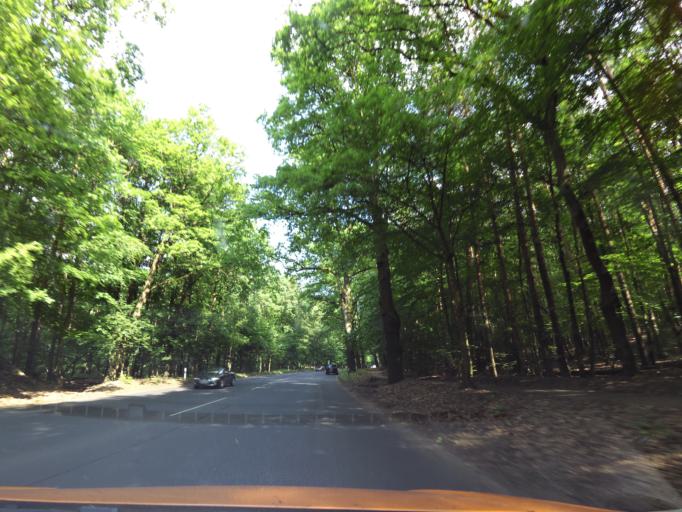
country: DE
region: Berlin
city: Heiligensee
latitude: 52.5993
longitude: 13.2585
